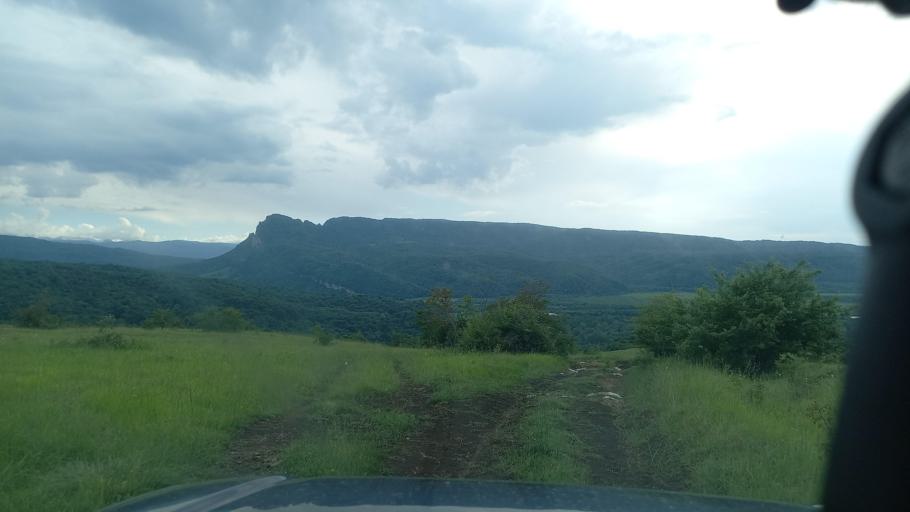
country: RU
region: Karachayevo-Cherkesiya
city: Kurdzhinovo
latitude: 44.1287
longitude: 41.0613
